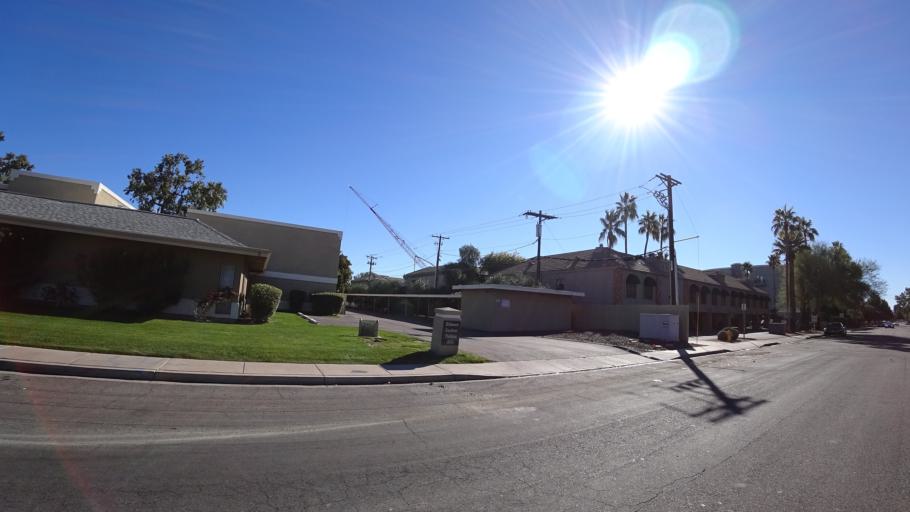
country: US
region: Arizona
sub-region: Maricopa County
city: Phoenix
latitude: 33.5041
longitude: -112.0346
